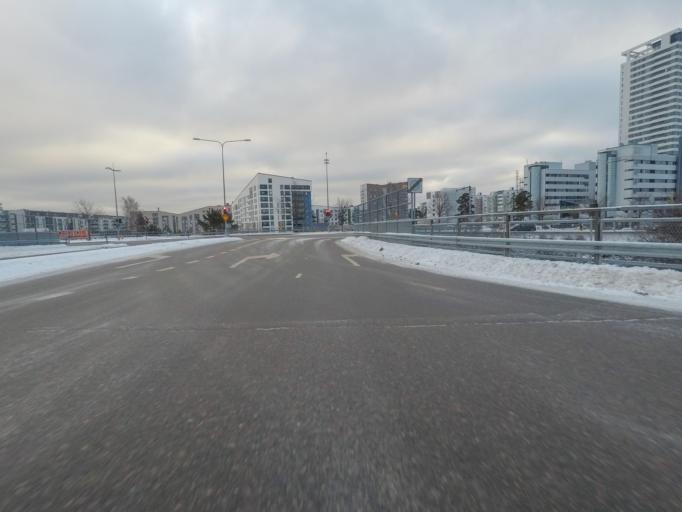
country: FI
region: Uusimaa
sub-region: Helsinki
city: Vantaa
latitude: 60.2078
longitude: 25.1484
